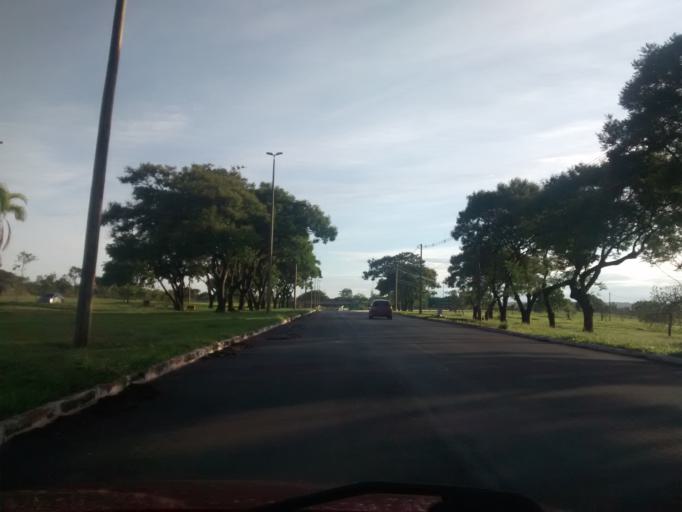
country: BR
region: Federal District
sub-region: Brasilia
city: Brasilia
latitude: -15.7779
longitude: -47.8669
